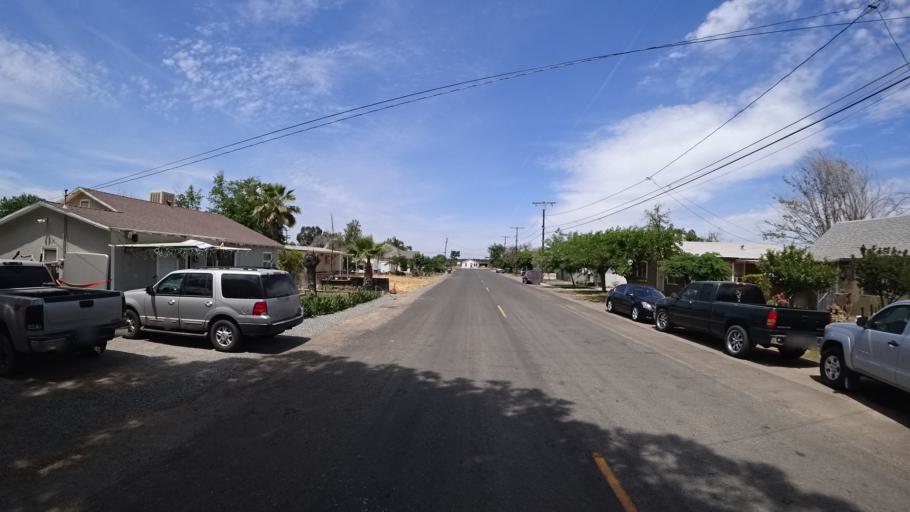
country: US
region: California
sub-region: Kings County
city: Armona
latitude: 36.3159
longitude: -119.7142
